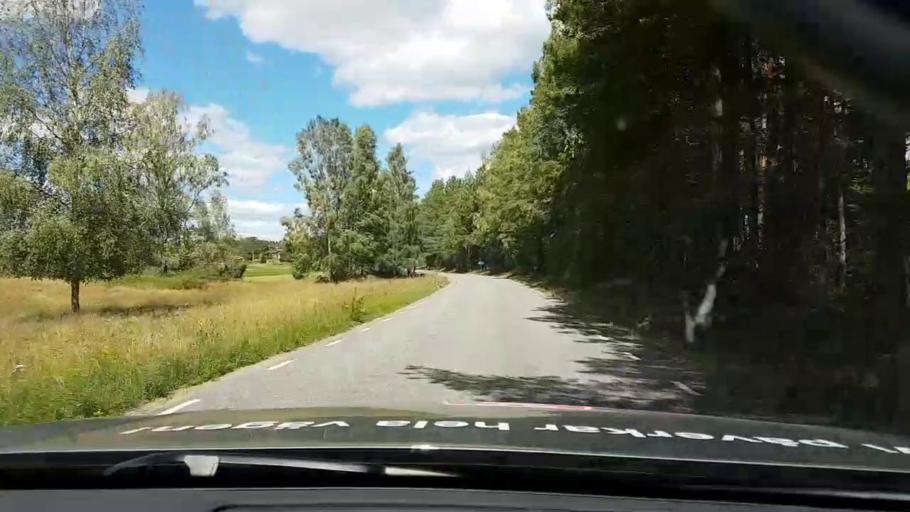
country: SE
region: Kalmar
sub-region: Vasterviks Kommun
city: Forserum
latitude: 58.0209
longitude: 16.5743
